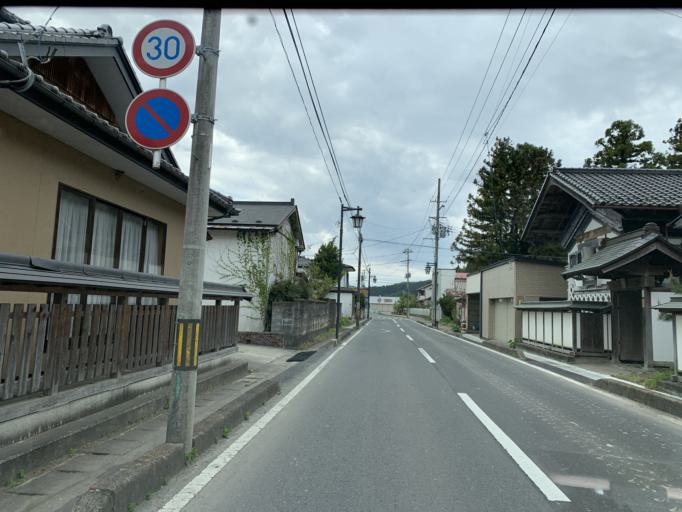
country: JP
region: Iwate
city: Ichinoseki
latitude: 38.7675
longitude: 141.3281
